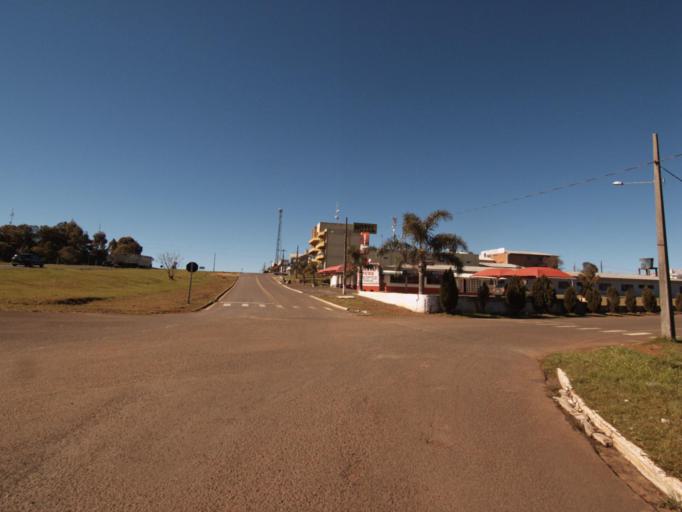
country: BR
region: Santa Catarina
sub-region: Xanxere
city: Xanxere
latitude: -26.8574
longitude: -52.2617
